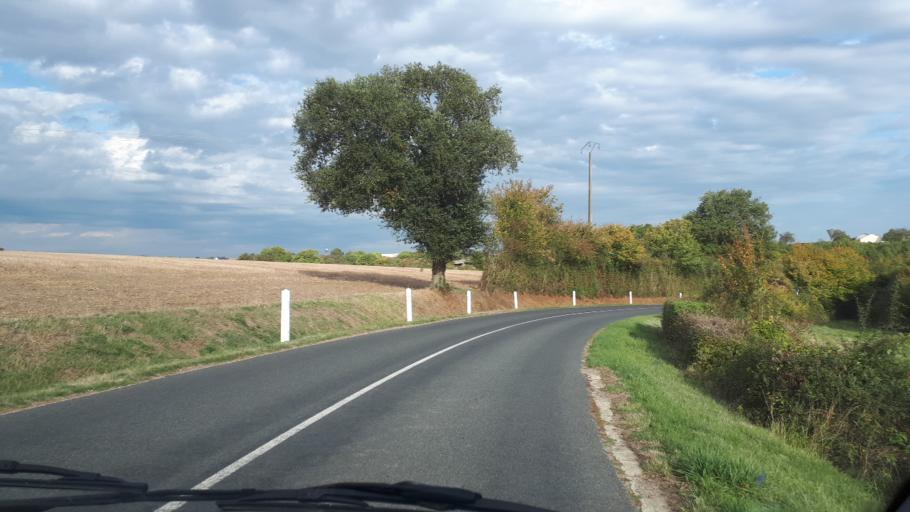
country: FR
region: Centre
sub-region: Departement du Loir-et-Cher
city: Mondoubleau
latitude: 47.9724
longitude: 0.9197
